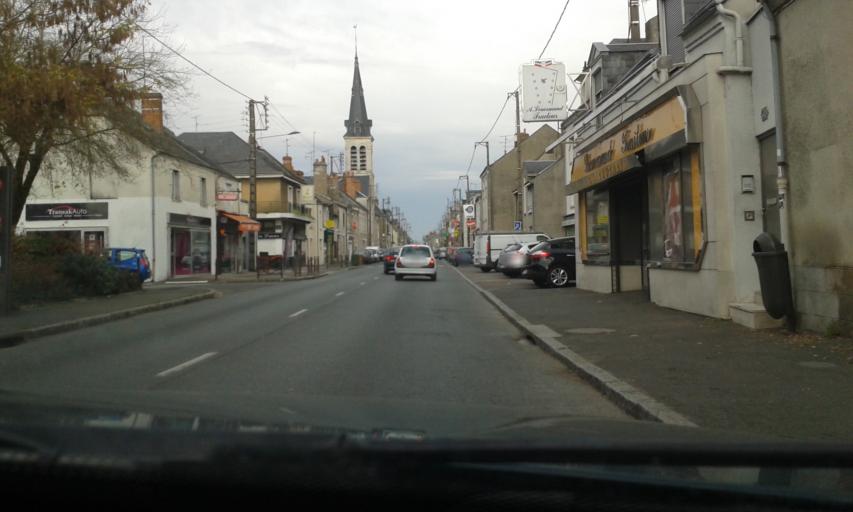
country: FR
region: Centre
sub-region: Departement du Loiret
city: Fleury-les-Aubrais
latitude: 47.9277
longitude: 1.8962
